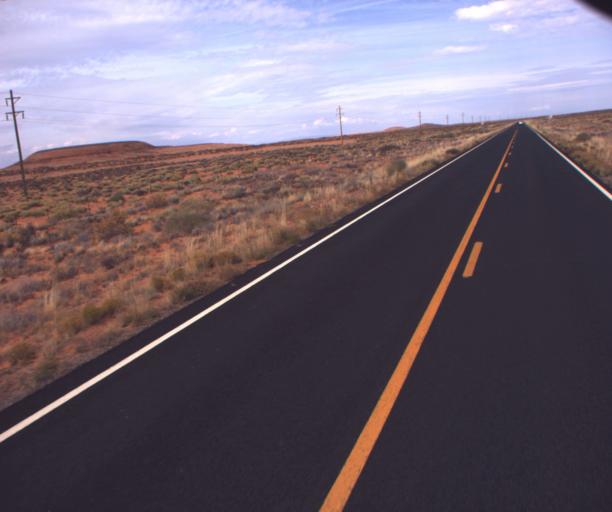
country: US
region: Arizona
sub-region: Apache County
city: Many Farms
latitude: 36.8261
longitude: -109.6444
